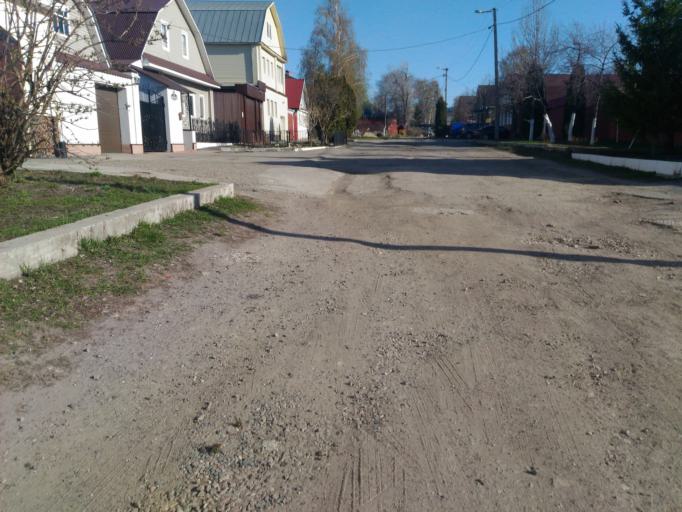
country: RU
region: Ulyanovsk
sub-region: Ulyanovskiy Rayon
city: Ulyanovsk
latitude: 54.3395
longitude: 48.3877
